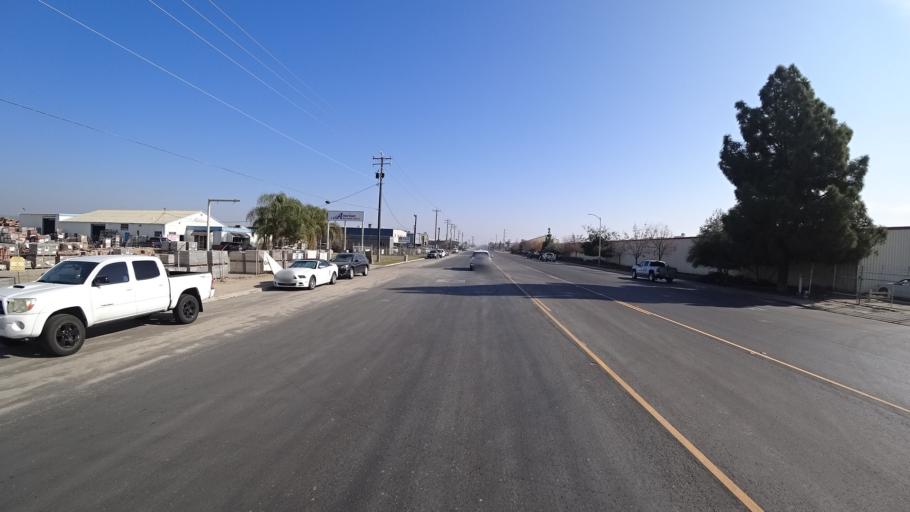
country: US
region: California
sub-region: Kern County
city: Bakersfield
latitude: 35.3541
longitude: -118.9619
